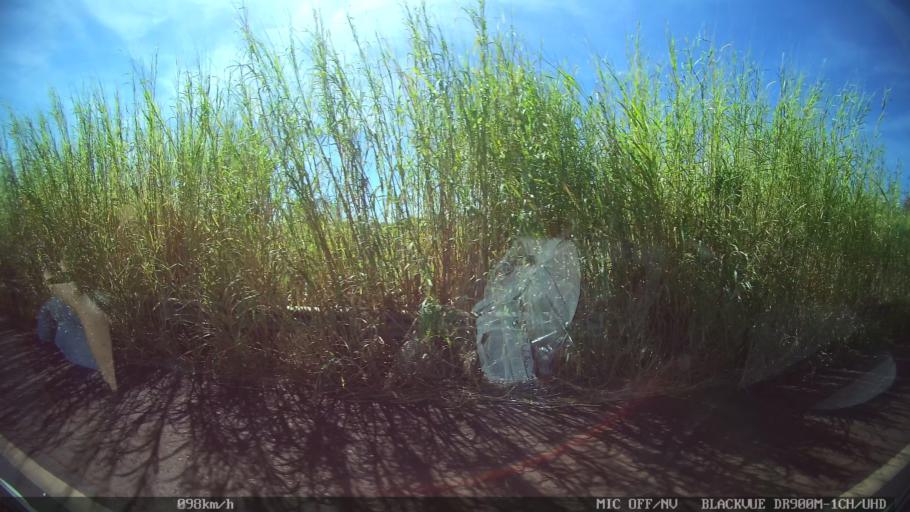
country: BR
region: Sao Paulo
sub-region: Nuporanga
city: Nuporanga
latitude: -20.5600
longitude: -47.6336
